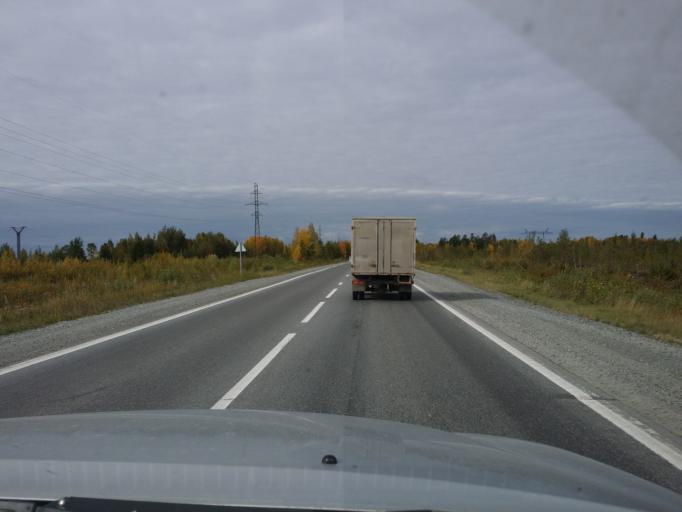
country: RU
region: Khanty-Mansiyskiy Avtonomnyy Okrug
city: Megion
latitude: 61.1041
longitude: 75.9389
